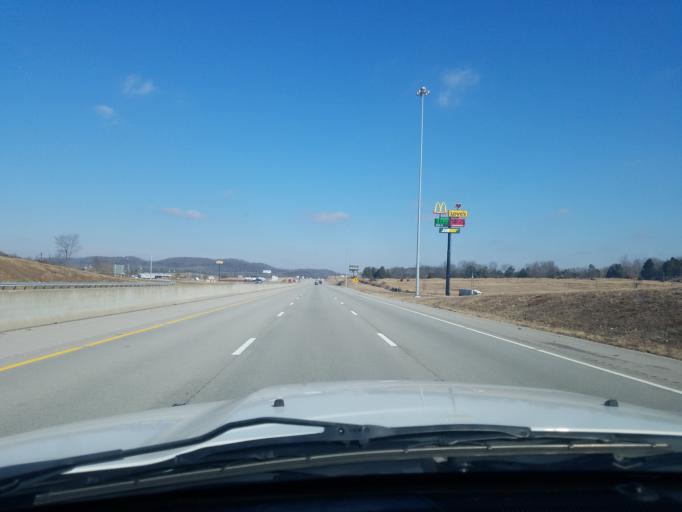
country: US
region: Kentucky
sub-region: Hart County
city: Horse Cave
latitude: 37.2017
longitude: -85.9374
